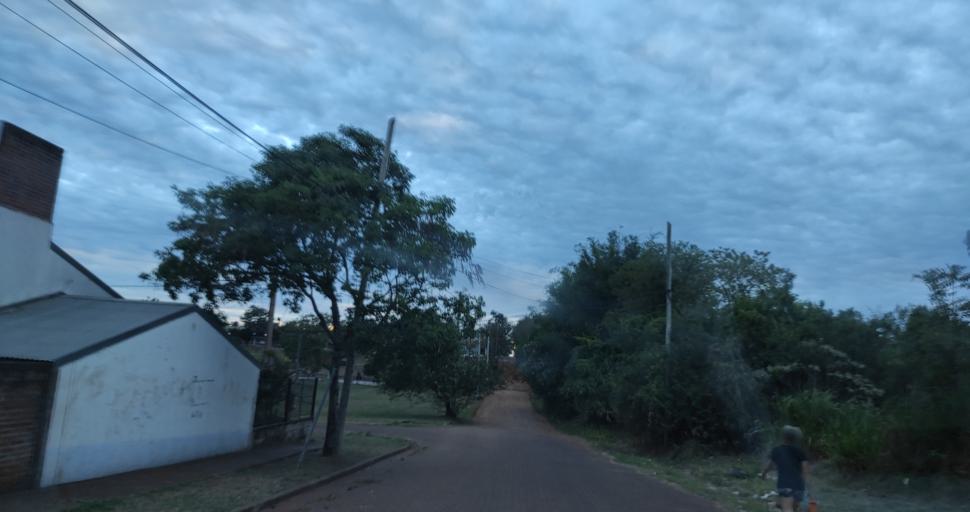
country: AR
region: Misiones
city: Garupa
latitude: -27.4704
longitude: -55.8470
